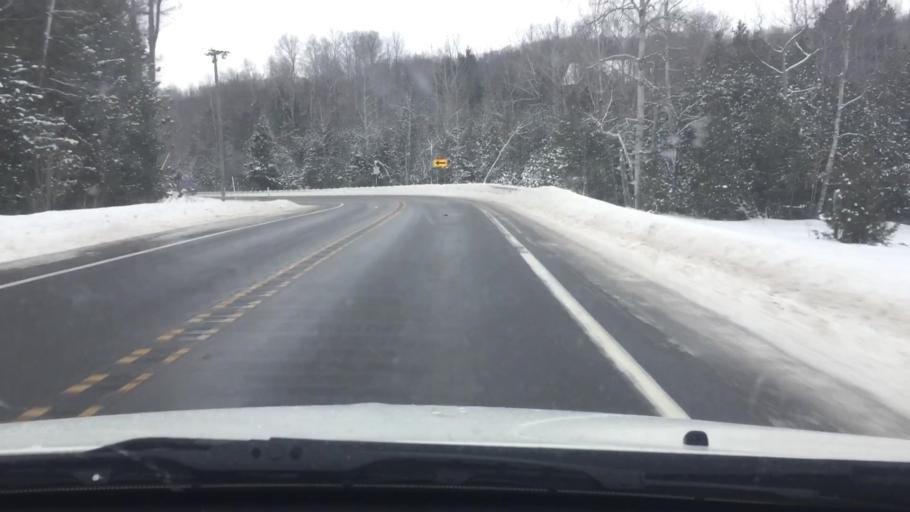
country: US
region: Michigan
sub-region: Charlevoix County
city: East Jordan
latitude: 45.1153
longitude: -85.0602
